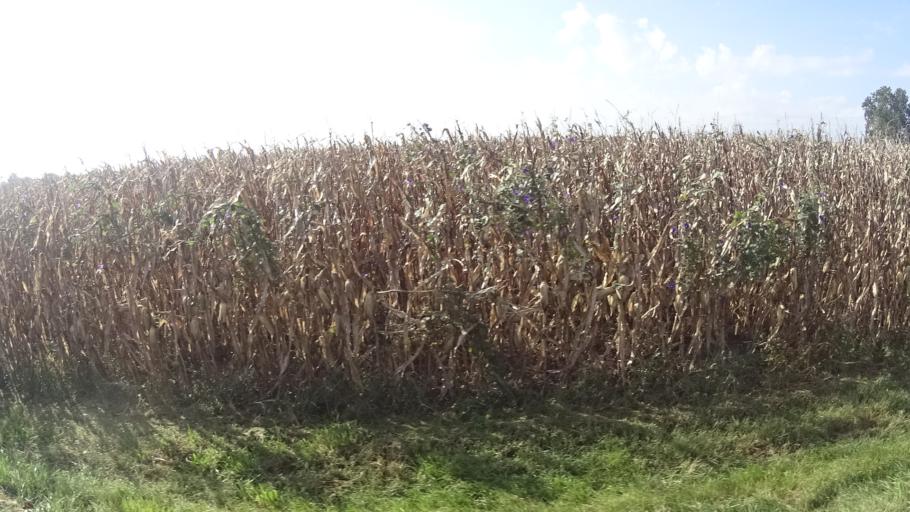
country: US
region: Indiana
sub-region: Madison County
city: Lapel
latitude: 40.0315
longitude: -85.8396
